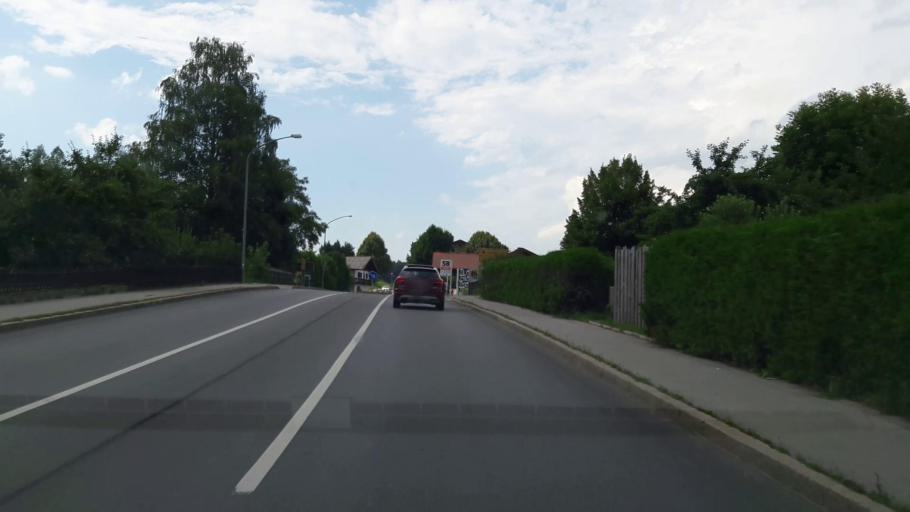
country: DE
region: Bavaria
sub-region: Upper Bavaria
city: Anger
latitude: 47.8007
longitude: 12.8657
